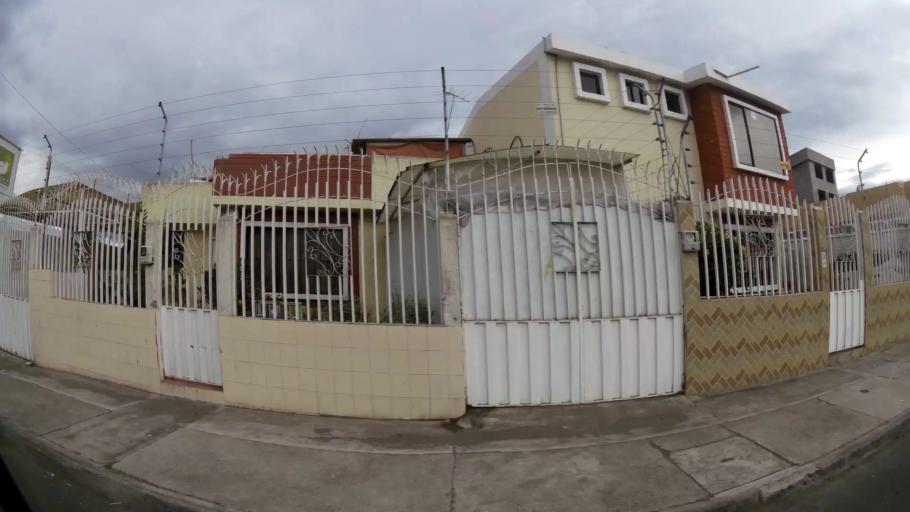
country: EC
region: Tungurahua
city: Ambato
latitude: -1.2791
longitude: -78.6195
